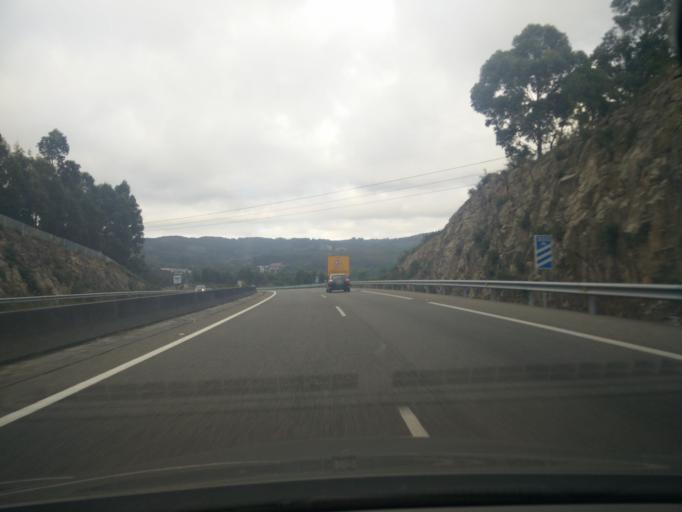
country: ES
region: Galicia
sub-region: Provincia da Coruna
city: Arteixo
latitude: 43.2979
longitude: -8.4789
